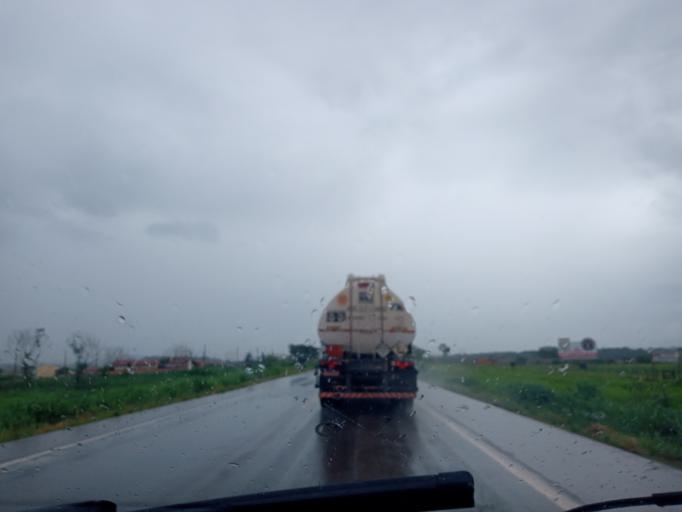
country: BR
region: Minas Gerais
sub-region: Luz
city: Luz
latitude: -19.7833
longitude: -45.6889
